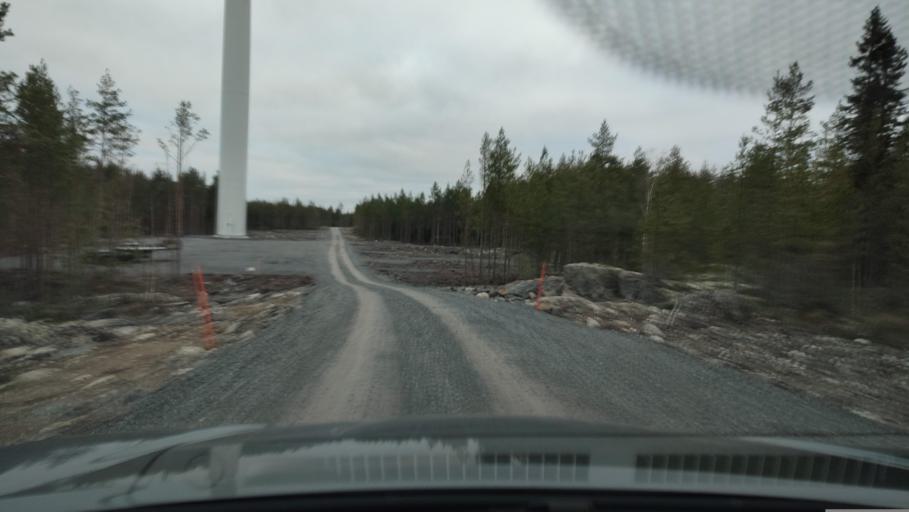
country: FI
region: Southern Ostrobothnia
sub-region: Suupohja
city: Karijoki
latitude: 62.1854
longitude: 21.5739
